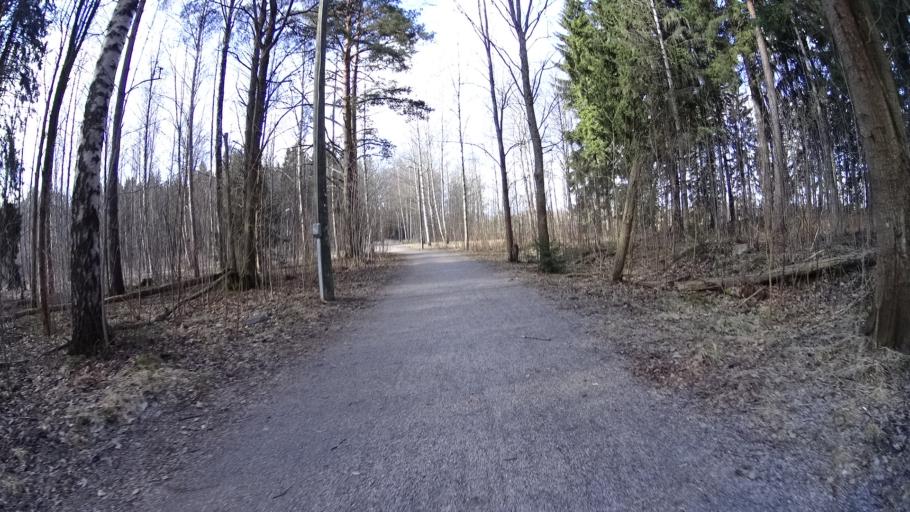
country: FI
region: Uusimaa
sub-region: Helsinki
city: Teekkarikylae
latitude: 60.2127
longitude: 24.8720
